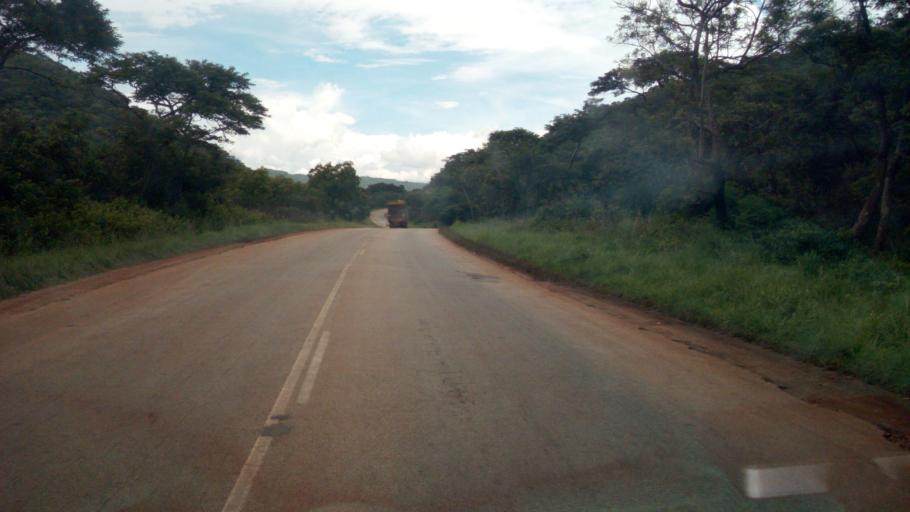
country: ZW
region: Mashonaland Central
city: Mazowe
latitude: -17.5149
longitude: 30.9815
